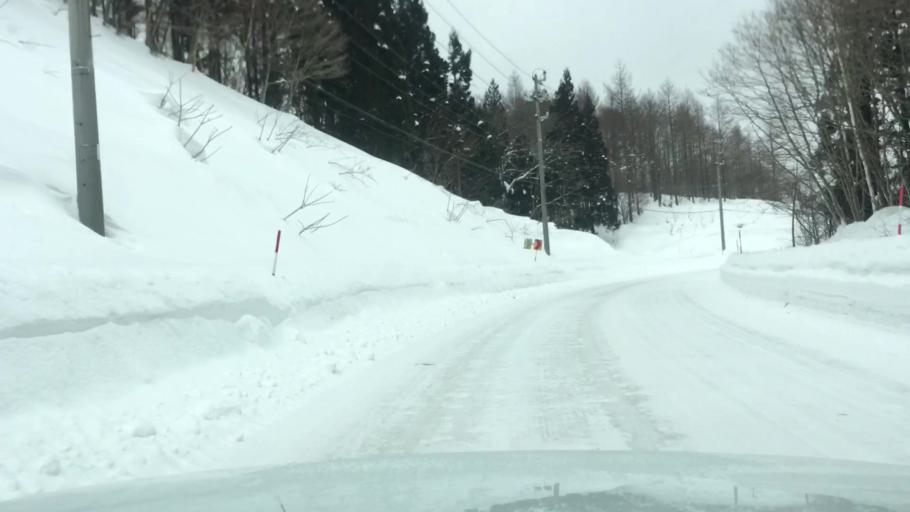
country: JP
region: Akita
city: Hanawa
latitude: 40.0003
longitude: 140.9863
